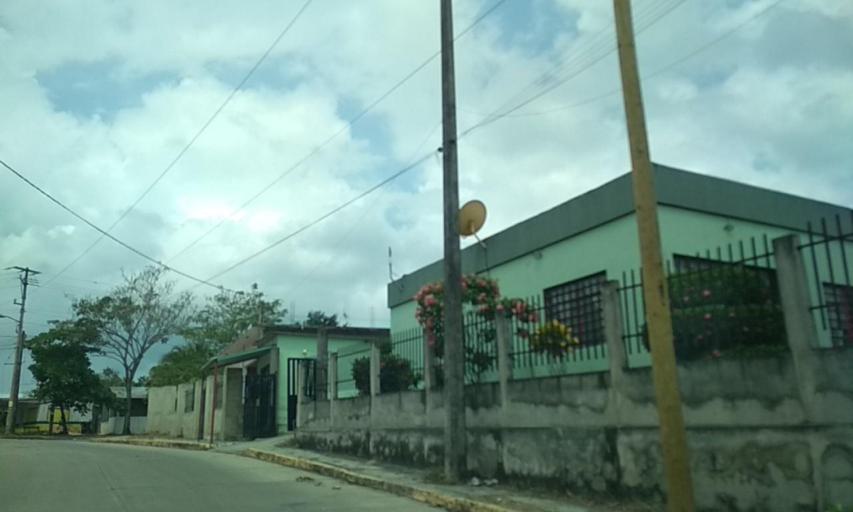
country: MX
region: Veracruz
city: Las Choapas
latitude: 17.8935
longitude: -94.1076
